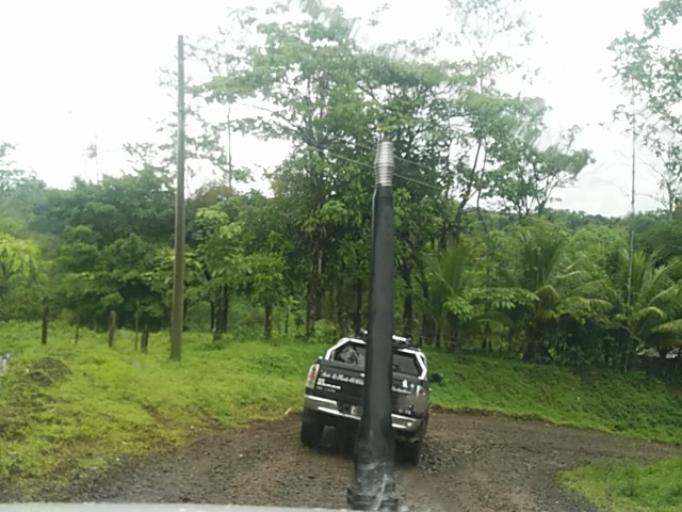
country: NI
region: Matagalpa
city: Rio Blanco
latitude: 13.0045
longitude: -85.2019
